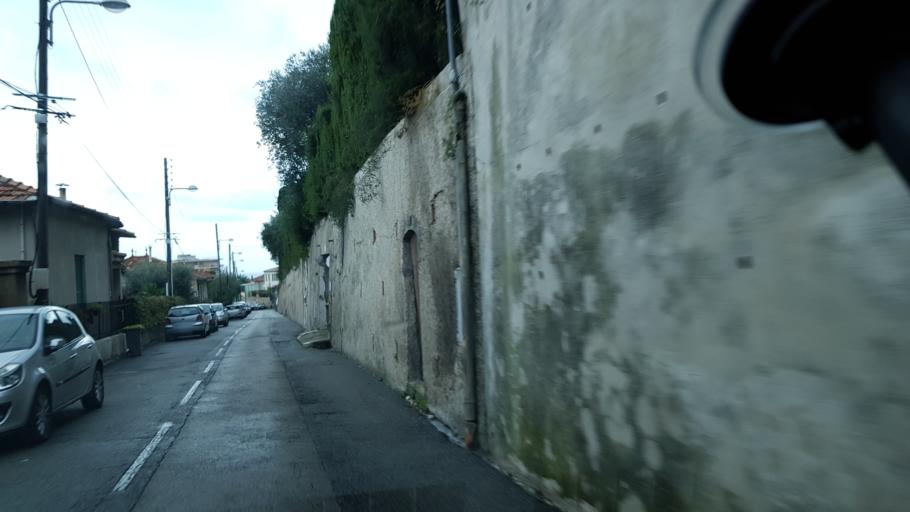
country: FR
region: Provence-Alpes-Cote d'Azur
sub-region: Departement des Alpes-Maritimes
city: Nice
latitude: 43.7010
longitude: 7.2335
